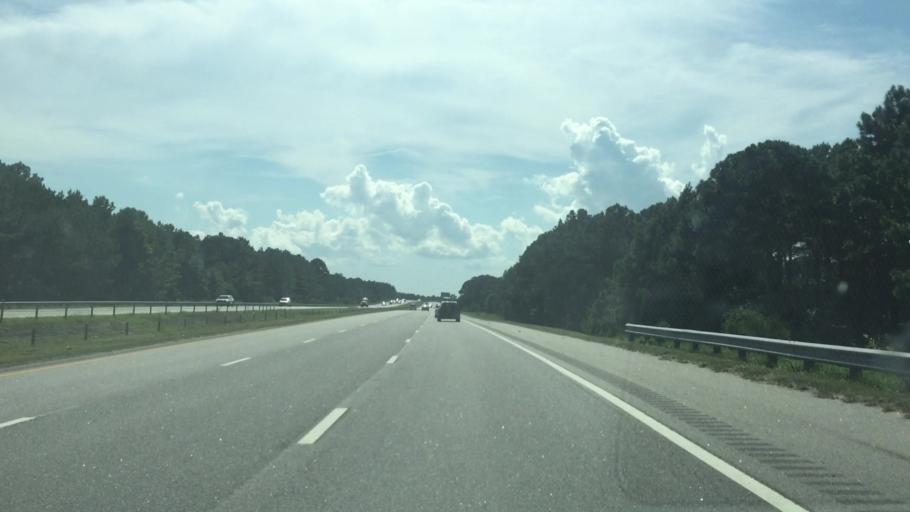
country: US
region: South Carolina
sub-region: Horry County
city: North Myrtle Beach
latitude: 33.8132
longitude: -78.7604
